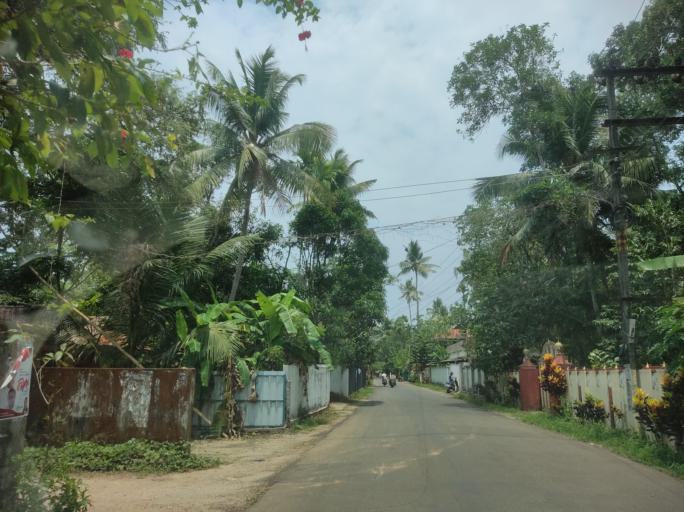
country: IN
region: Kerala
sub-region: Alappuzha
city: Vayalar
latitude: 9.7345
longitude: 76.3279
